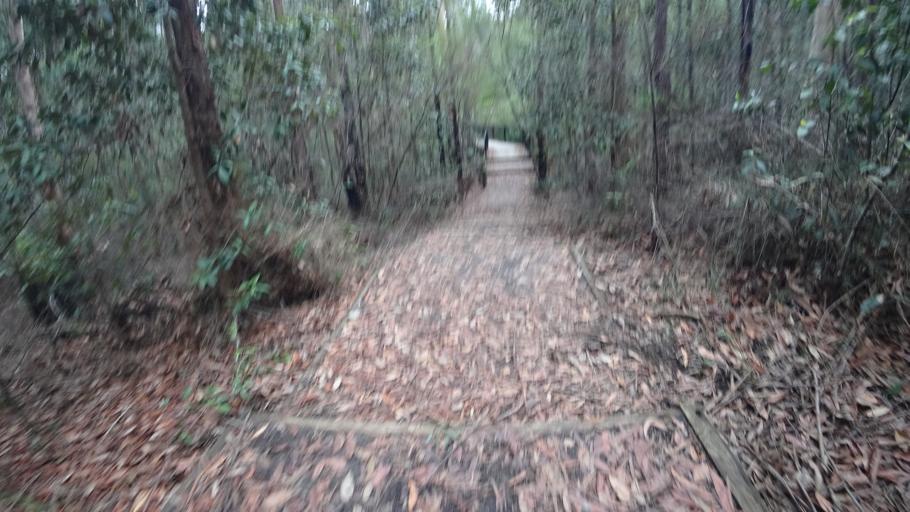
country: AU
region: New South Wales
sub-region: Shoalhaven Shire
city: Milton
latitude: -35.1652
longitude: 150.3779
